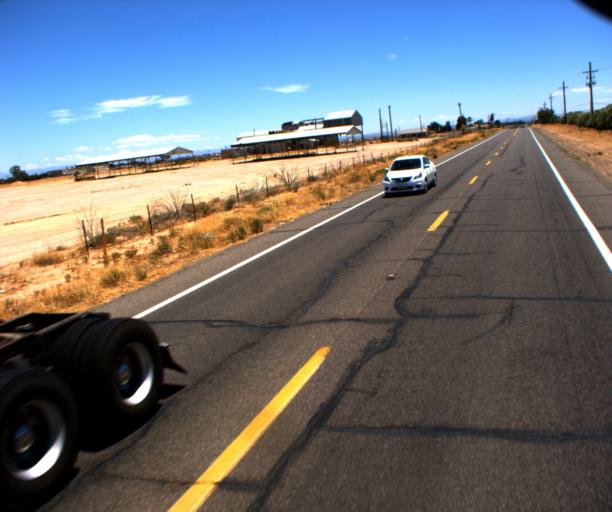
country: US
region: Arizona
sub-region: Pinal County
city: Coolidge
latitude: 32.8796
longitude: -111.5746
